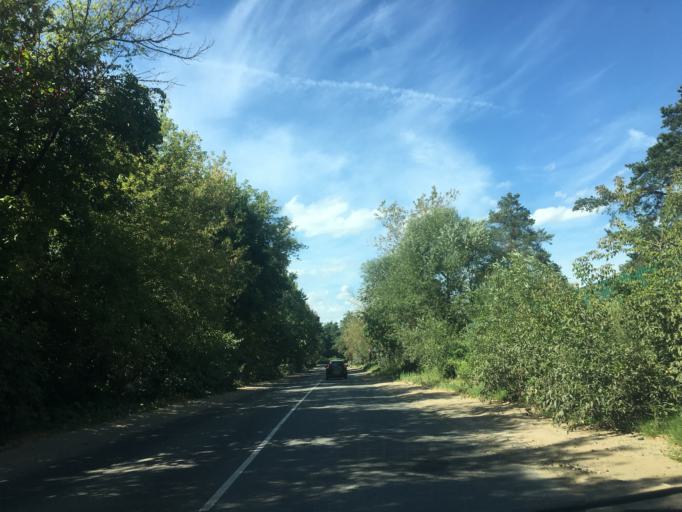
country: RU
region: Moskovskaya
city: Vidnoye
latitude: 55.5172
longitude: 37.6824
